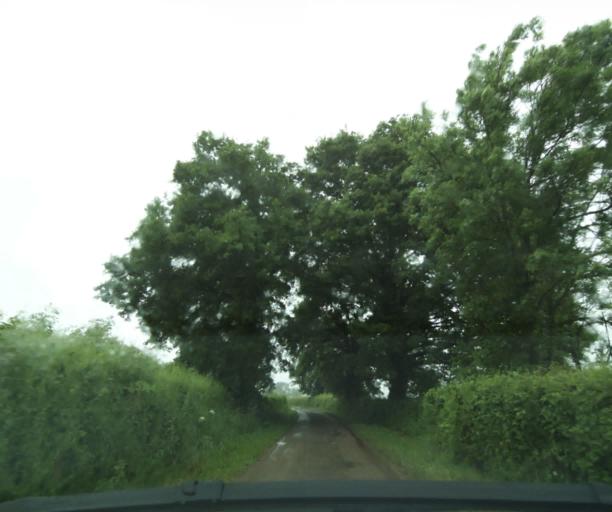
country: FR
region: Bourgogne
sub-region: Departement de Saone-et-Loire
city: Charolles
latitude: 46.3989
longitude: 4.2381
